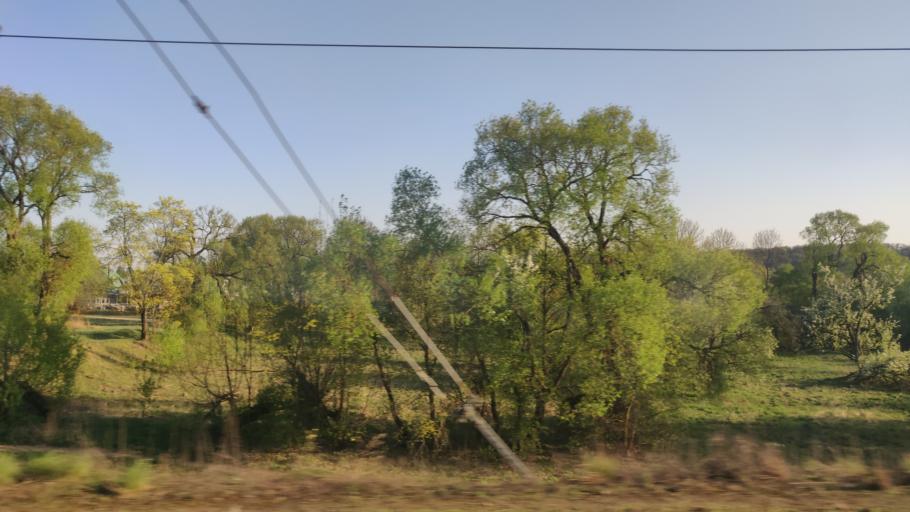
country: LT
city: Grigiskes
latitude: 54.6335
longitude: 25.1264
